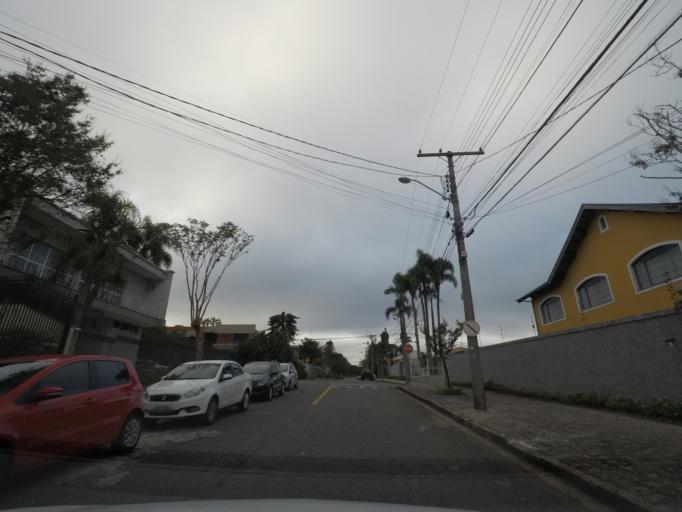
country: BR
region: Parana
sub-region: Curitiba
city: Curitiba
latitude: -25.4430
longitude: -49.2482
